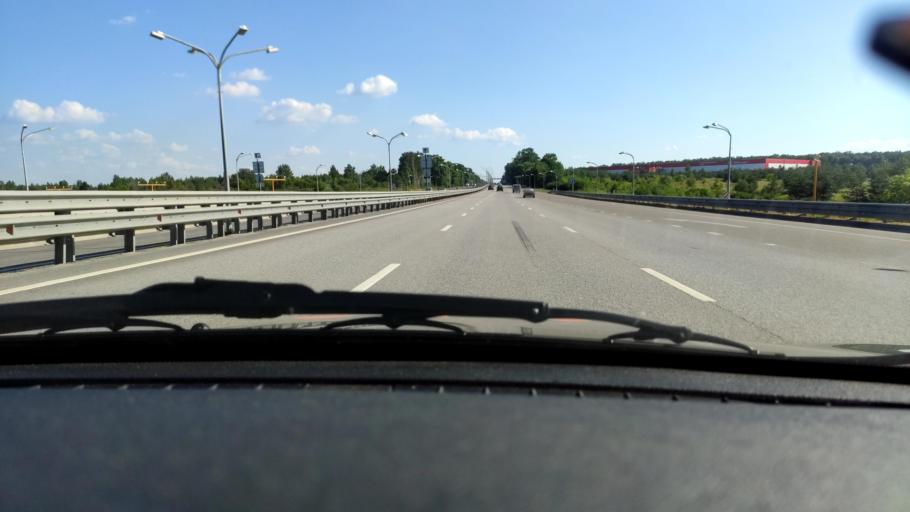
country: RU
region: Voronezj
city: Podgornoye
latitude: 51.8256
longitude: 39.2120
